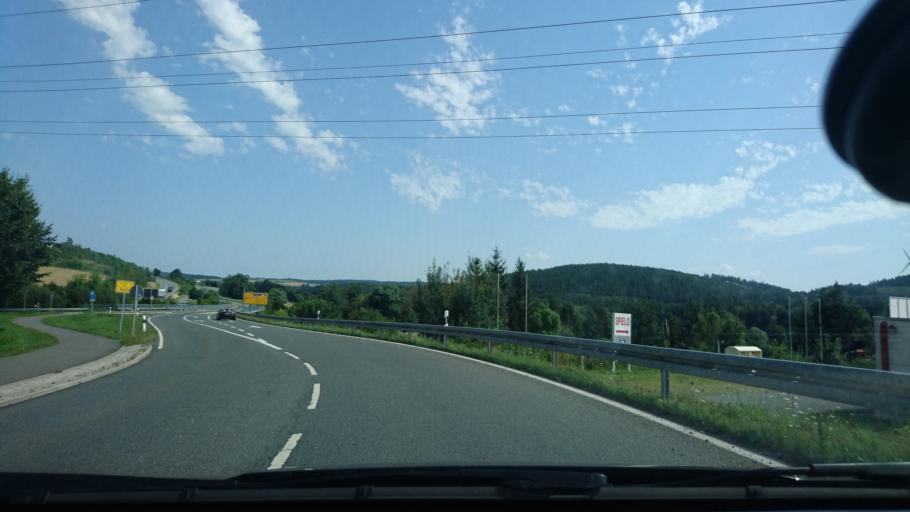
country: DE
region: Bavaria
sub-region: Upper Franconia
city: Naila
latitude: 50.3215
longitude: 11.7213
